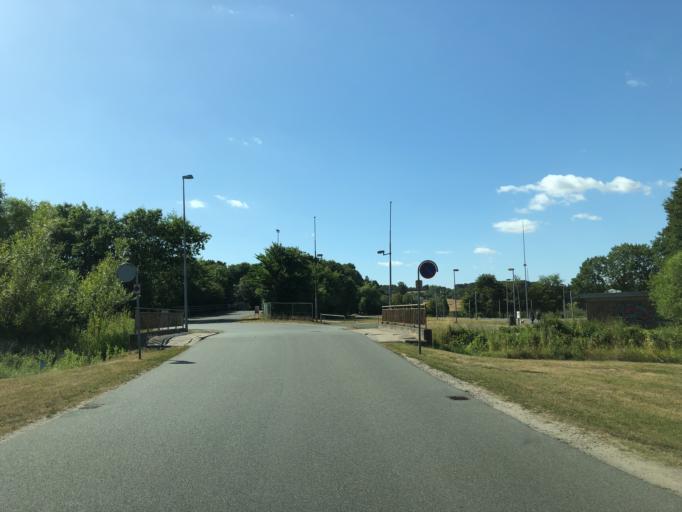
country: DK
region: North Denmark
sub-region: Mariagerfjord Kommune
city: Hobro
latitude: 56.6334
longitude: 9.7895
